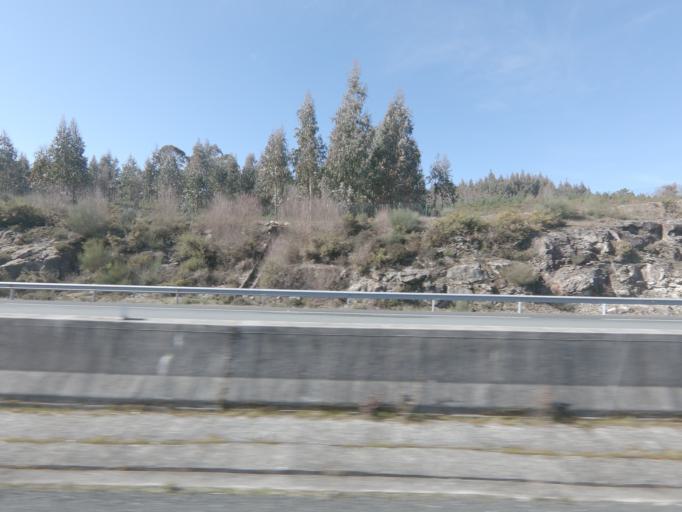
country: ES
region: Galicia
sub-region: Provincia de Ourense
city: Pinor
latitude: 42.5055
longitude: -8.0239
